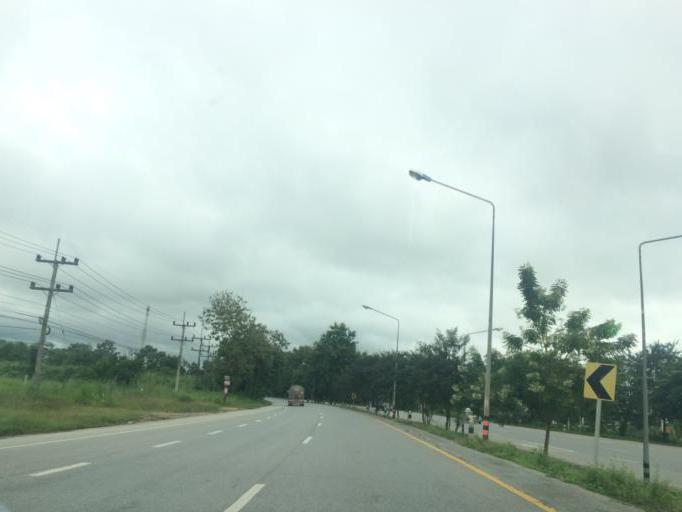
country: TH
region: Chiang Rai
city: Mae Lao
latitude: 19.7993
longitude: 99.7528
